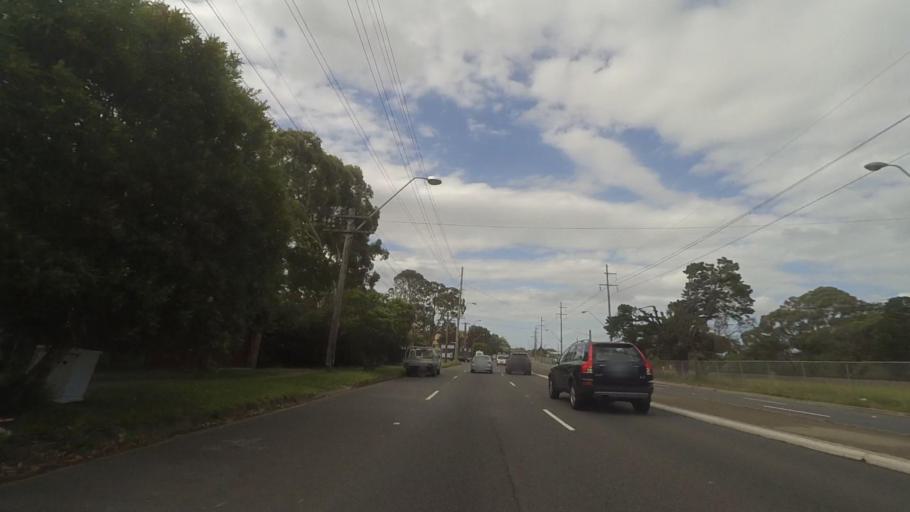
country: AU
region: New South Wales
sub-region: Sutherland Shire
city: Engadine
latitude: -34.0705
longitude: 151.0126
